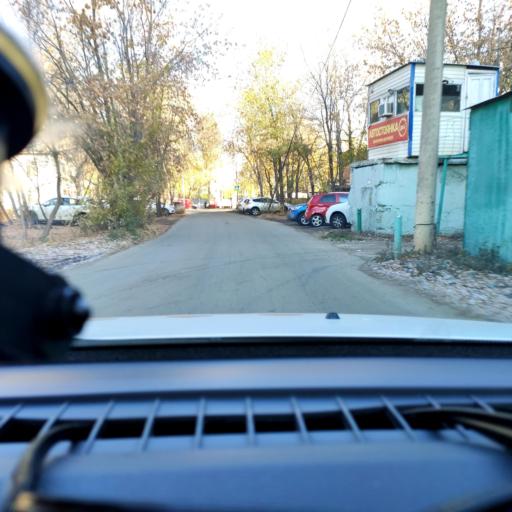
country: RU
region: Samara
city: Samara
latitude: 53.2048
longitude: 50.1857
